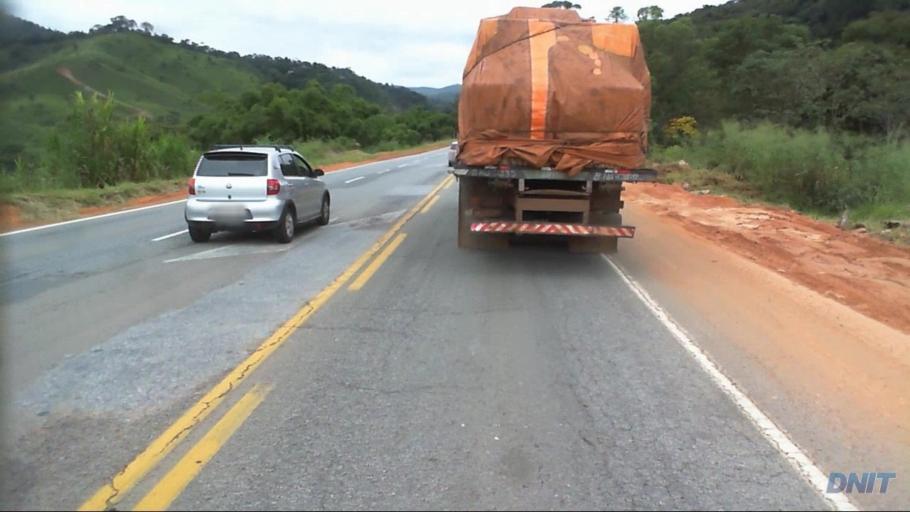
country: BR
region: Minas Gerais
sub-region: Joao Monlevade
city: Joao Monlevade
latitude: -19.8607
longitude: -43.2276
